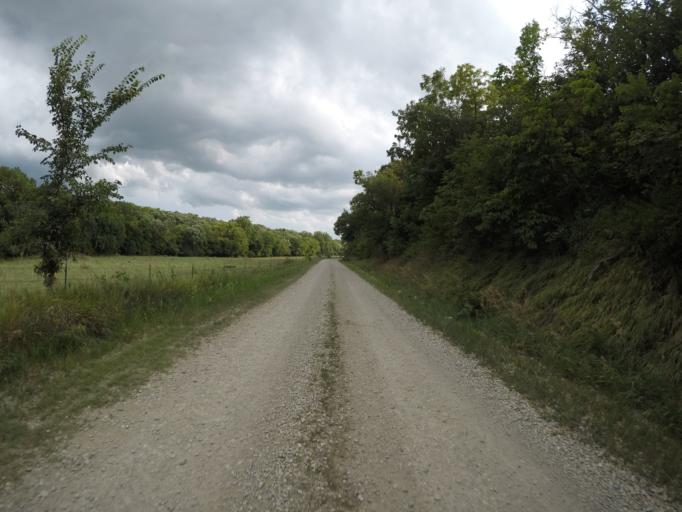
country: US
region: Kansas
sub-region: Marshall County
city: Blue Rapids
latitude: 39.5133
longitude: -96.8316
